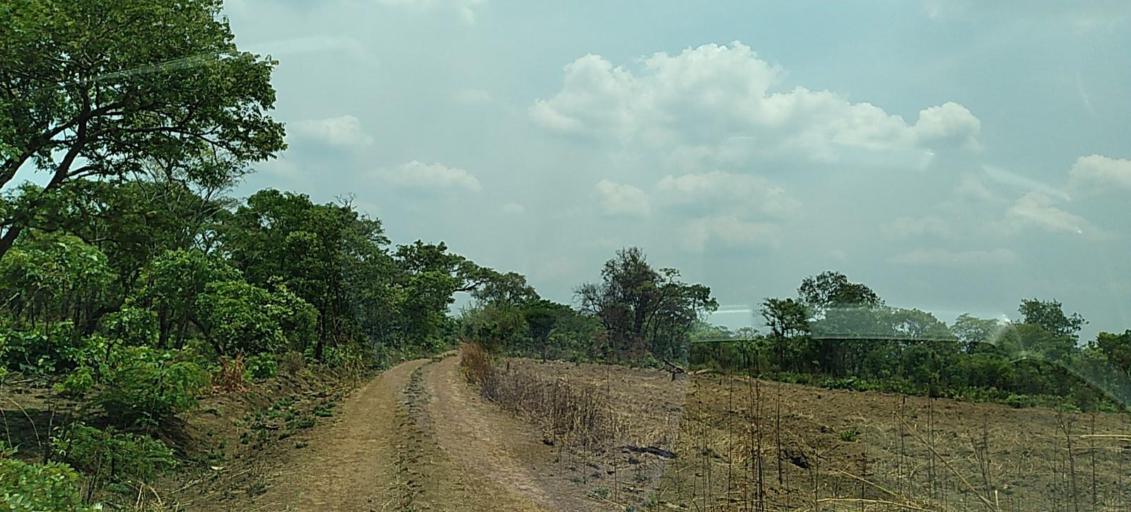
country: ZM
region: Copperbelt
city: Chililabombwe
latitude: -12.3798
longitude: 27.6442
